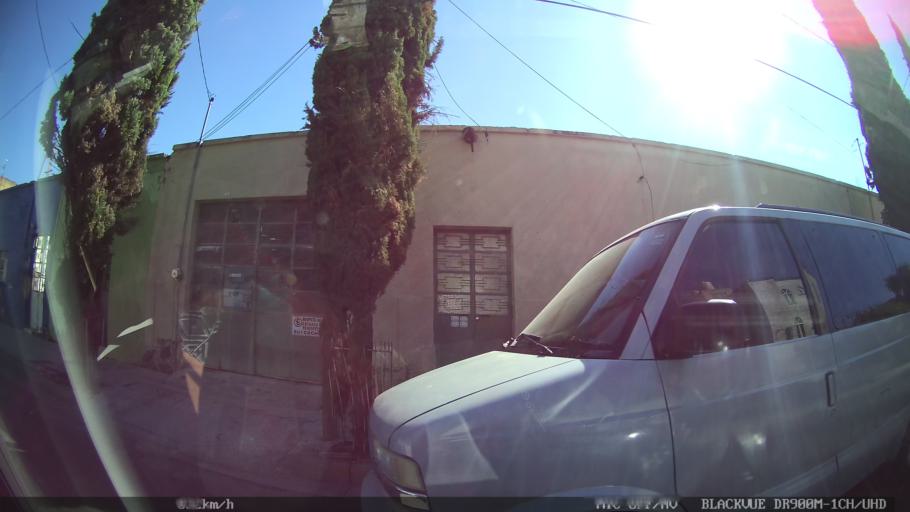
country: MX
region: Jalisco
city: Tlaquepaque
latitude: 20.6714
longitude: -103.2804
